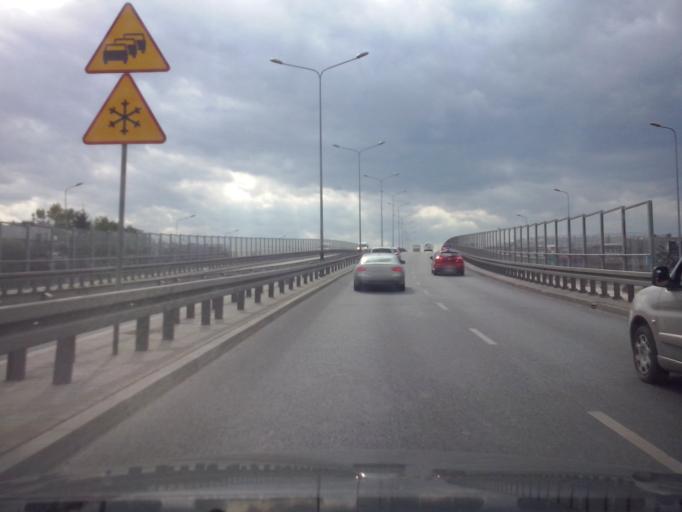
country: PL
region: Lesser Poland Voivodeship
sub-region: Krakow
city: Krakow
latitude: 50.0462
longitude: 19.9760
